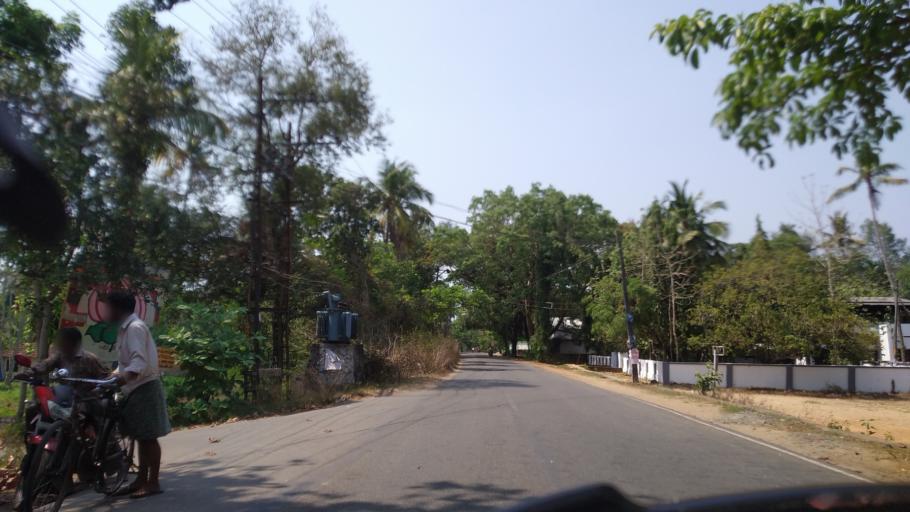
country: IN
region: Kerala
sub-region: Thrissur District
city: Kodungallur
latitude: 10.2020
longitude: 76.1678
